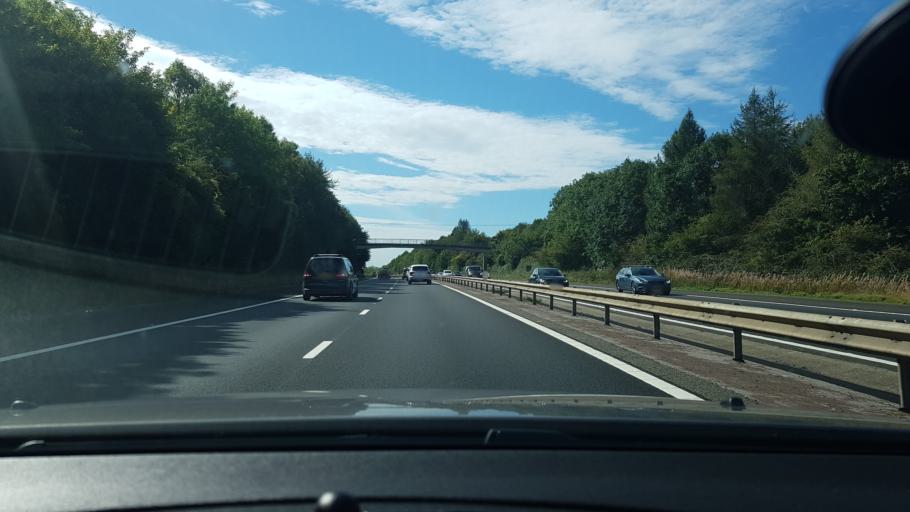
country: GB
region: England
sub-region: Hampshire
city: Overton
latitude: 51.1930
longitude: -1.2040
